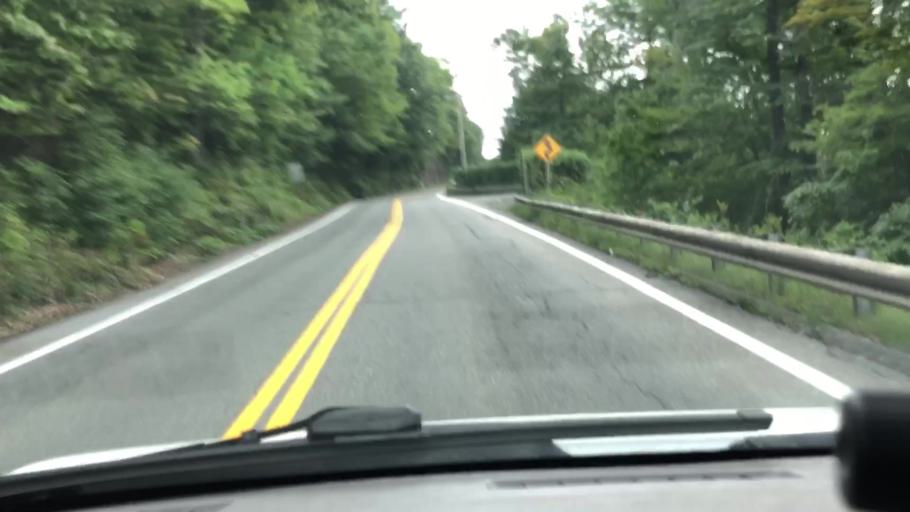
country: US
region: Massachusetts
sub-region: Berkshire County
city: North Adams
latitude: 42.7082
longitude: -73.0632
